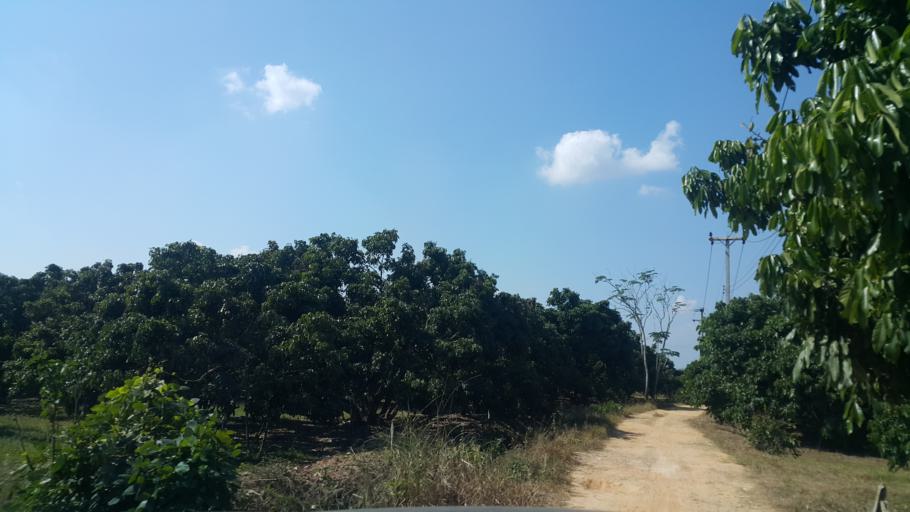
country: TH
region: Lamphun
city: Ban Thi
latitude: 18.6296
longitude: 99.1571
